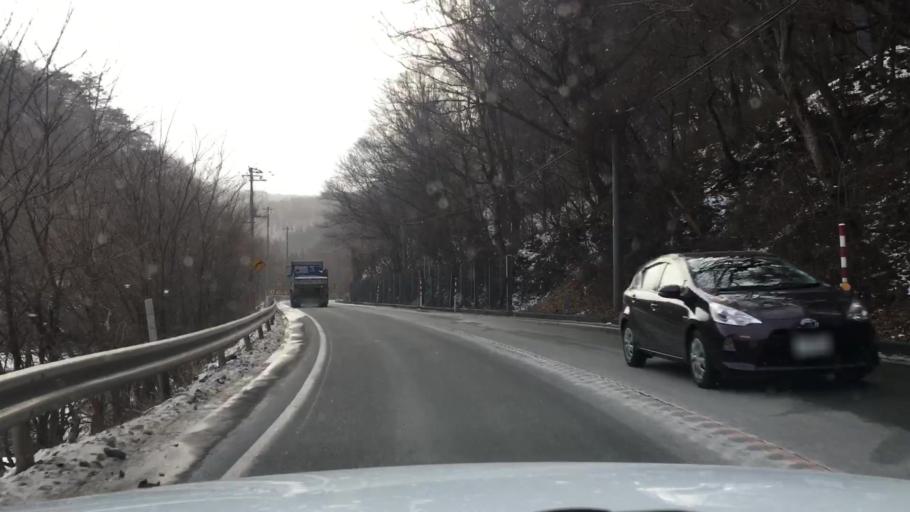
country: JP
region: Iwate
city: Tono
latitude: 39.6163
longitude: 141.4877
